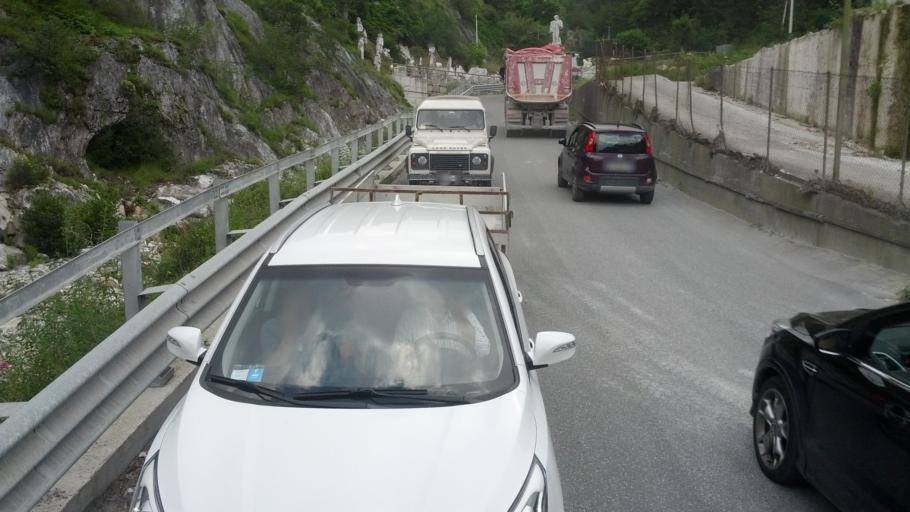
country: IT
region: Tuscany
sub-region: Provincia di Massa-Carrara
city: Massa
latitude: 44.0801
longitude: 10.1279
